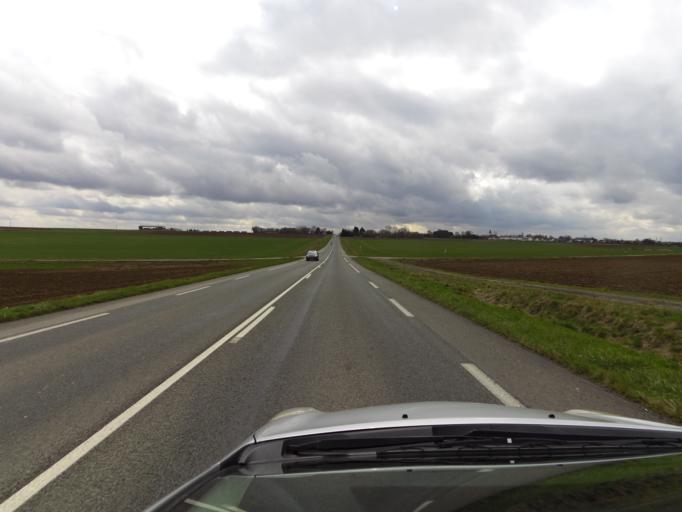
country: FR
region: Nord-Pas-de-Calais
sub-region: Departement du Pas-de-Calais
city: Beaurains
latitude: 50.2448
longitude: 2.7955
